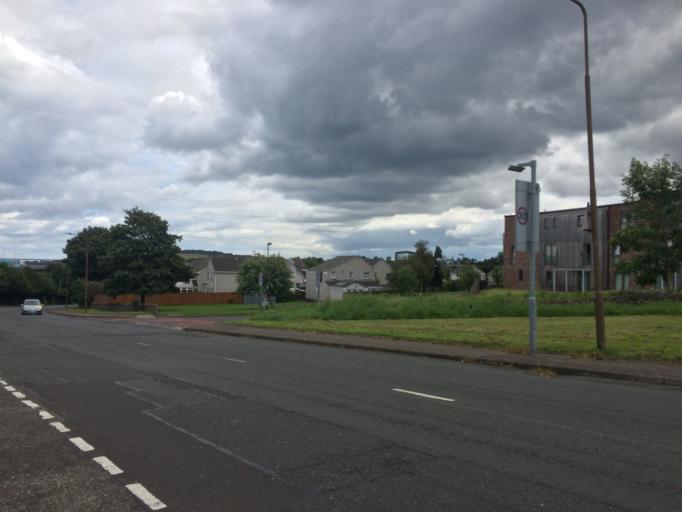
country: GB
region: Scotland
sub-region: Edinburgh
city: Queensferry
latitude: 55.9893
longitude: -3.4108
